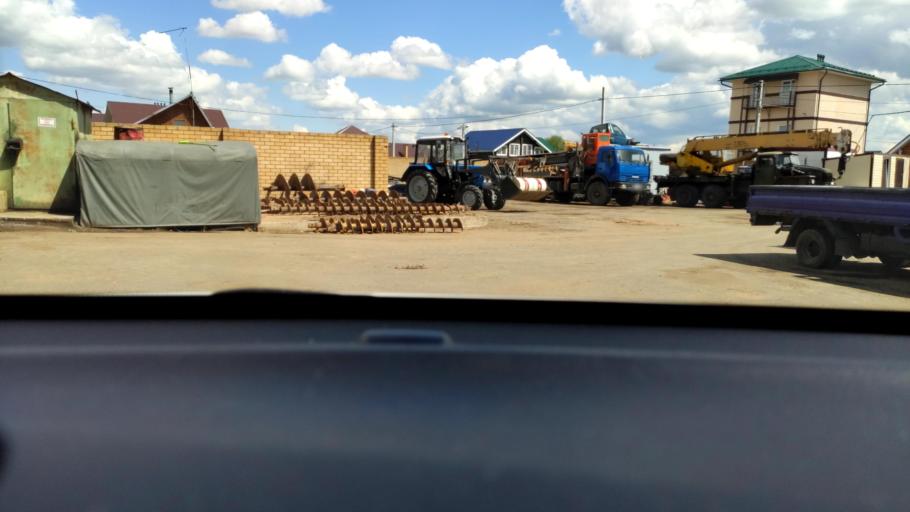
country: RU
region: Tatarstan
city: Stolbishchi
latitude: 55.7499
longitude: 49.2607
